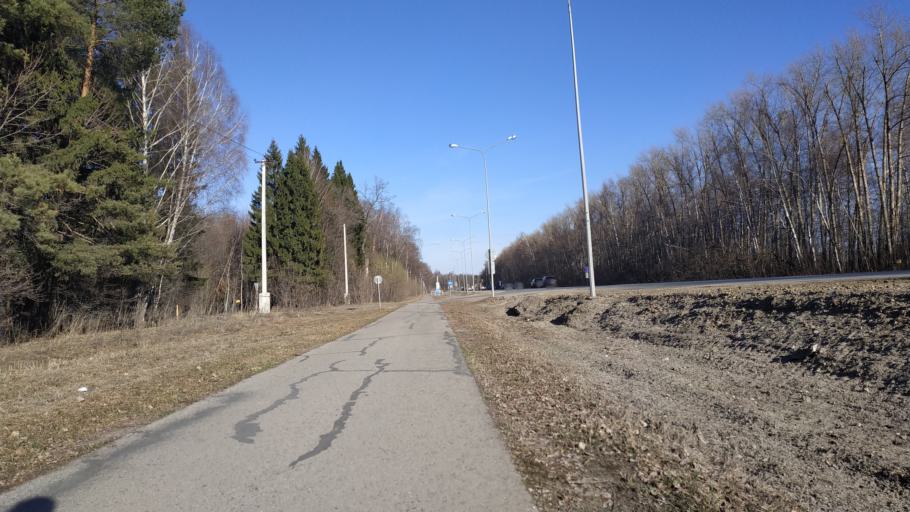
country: RU
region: Chuvashia
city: Ishley
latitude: 56.1344
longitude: 47.0994
